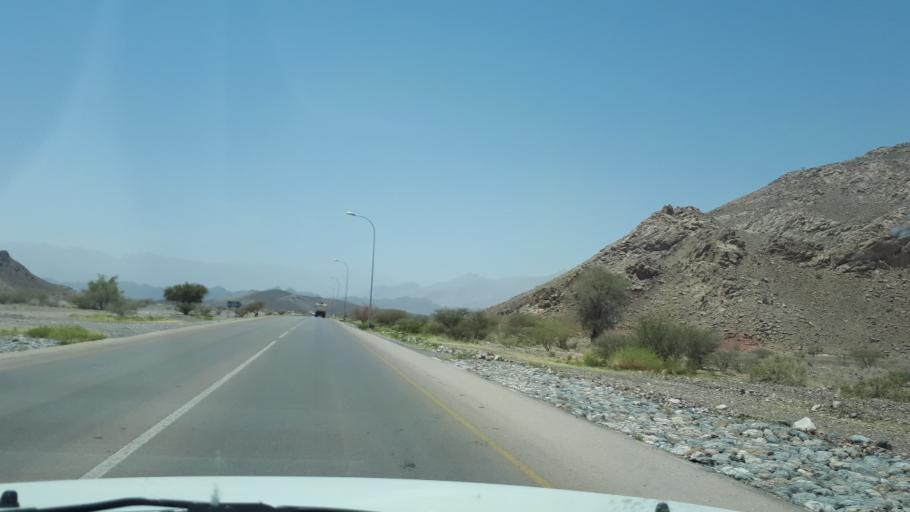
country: OM
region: Muhafazat ad Dakhiliyah
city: Bahla'
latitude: 23.0547
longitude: 57.2964
